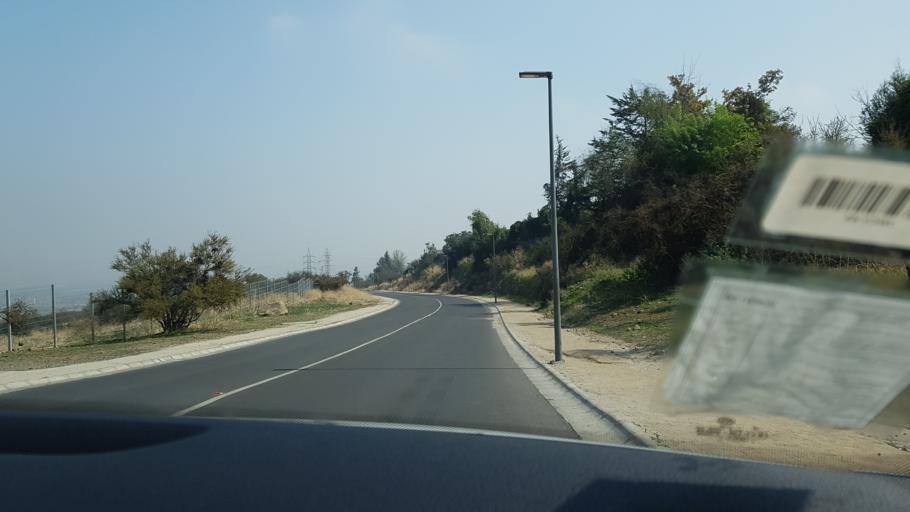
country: CL
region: Santiago Metropolitan
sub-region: Provincia de Santiago
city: Villa Presidente Frei, Nunoa, Santiago, Chile
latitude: -33.4806
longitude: -70.5198
